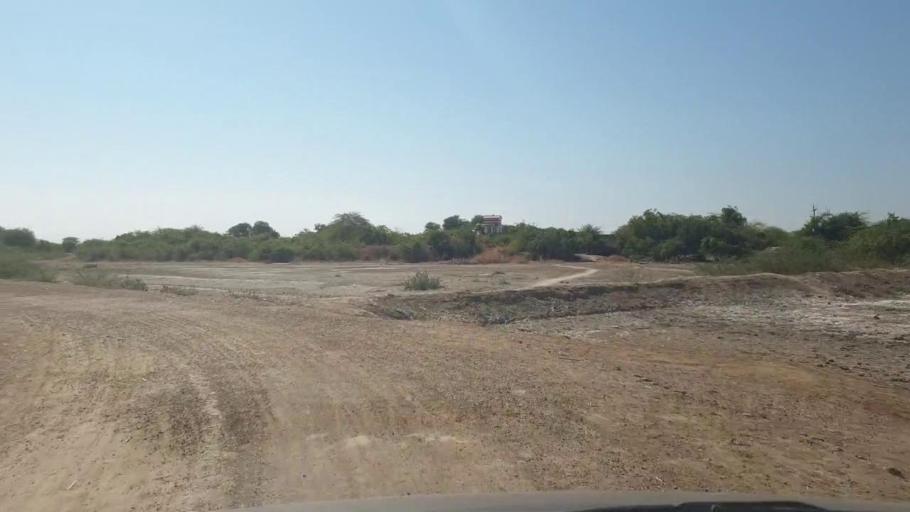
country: PK
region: Sindh
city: Umarkot
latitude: 25.3871
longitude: 69.6199
